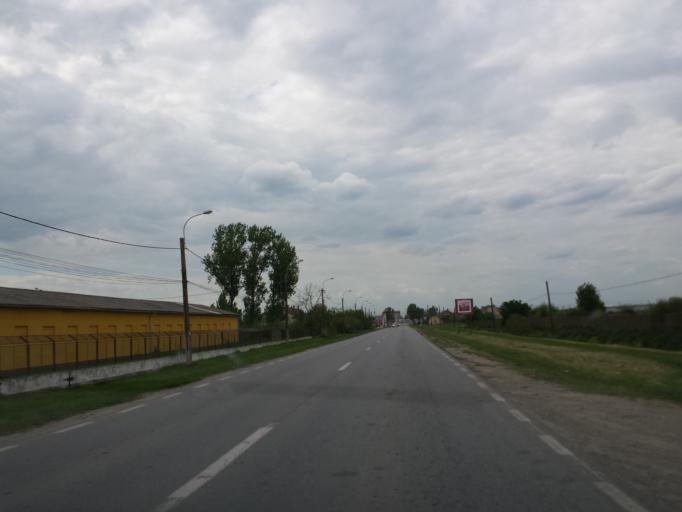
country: RO
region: Timis
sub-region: Comuna Sanpetru Mare
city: Sanpetru Mare
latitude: 46.0525
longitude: 20.6460
